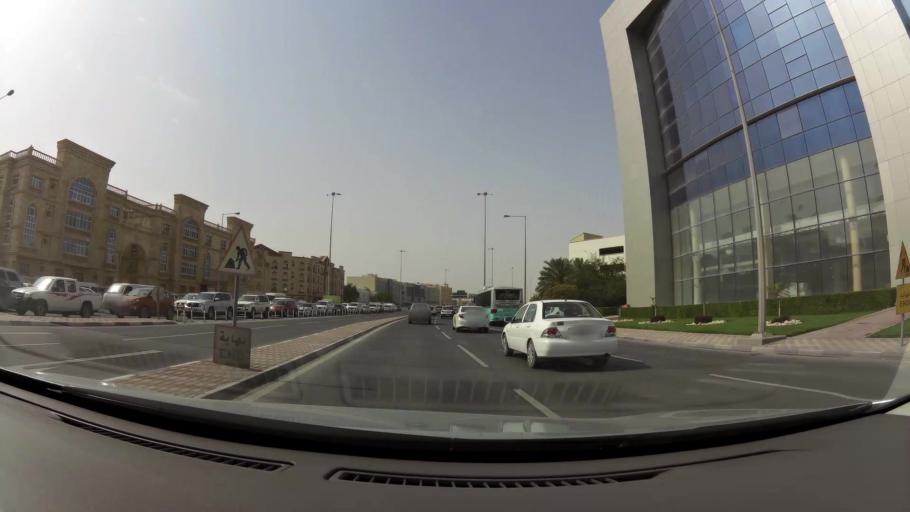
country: QA
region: Baladiyat ad Dawhah
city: Doha
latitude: 25.2798
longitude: 51.4937
